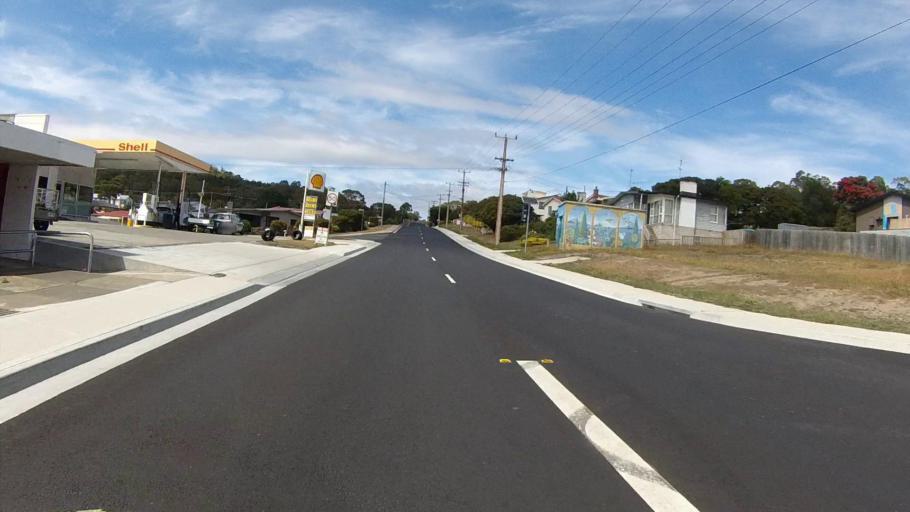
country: AU
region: Tasmania
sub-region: Clarence
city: Lindisfarne
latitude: -42.8129
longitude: 147.3513
